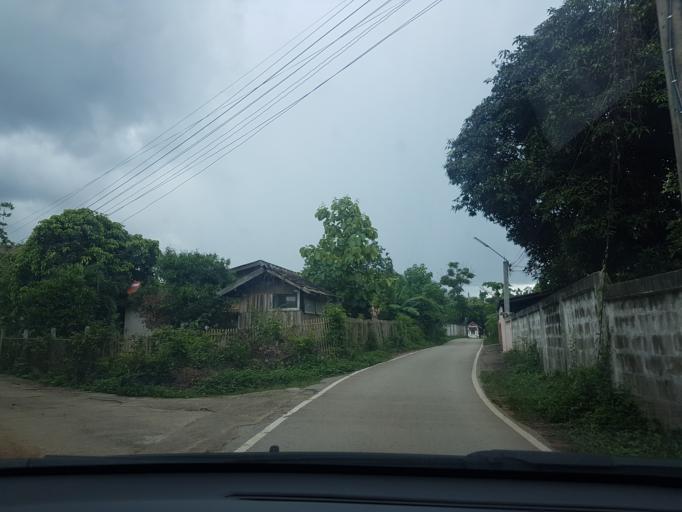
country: TH
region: Lampang
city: Ko Kha
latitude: 18.2211
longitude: 99.4156
